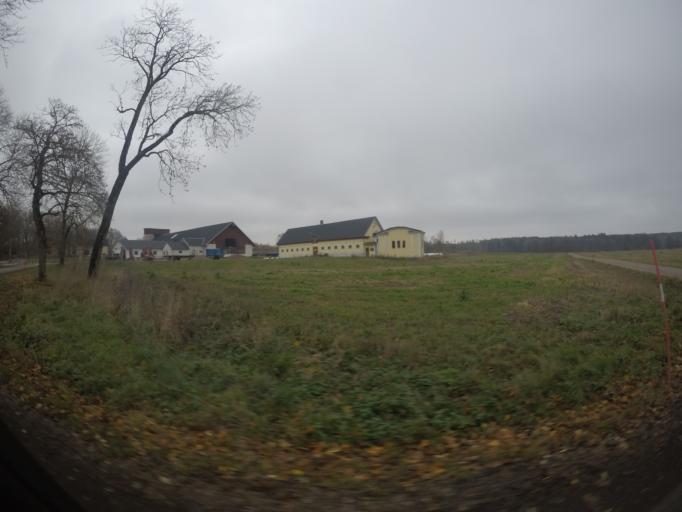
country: SE
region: Vaestmanland
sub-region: Surahammars Kommun
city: Ramnas
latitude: 59.6951
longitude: 16.0657
